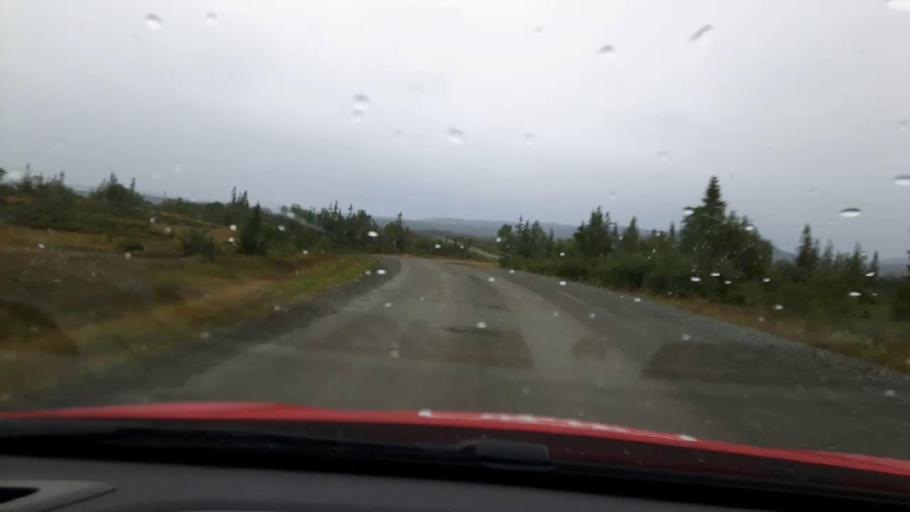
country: NO
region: Nord-Trondelag
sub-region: Meraker
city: Meraker
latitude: 63.5940
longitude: 12.2716
